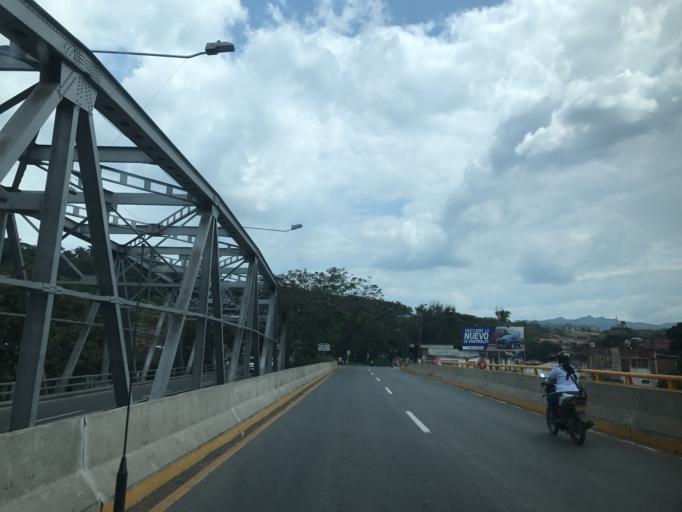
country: CO
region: Valle del Cauca
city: Cartago
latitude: 4.7583
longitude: -75.8992
